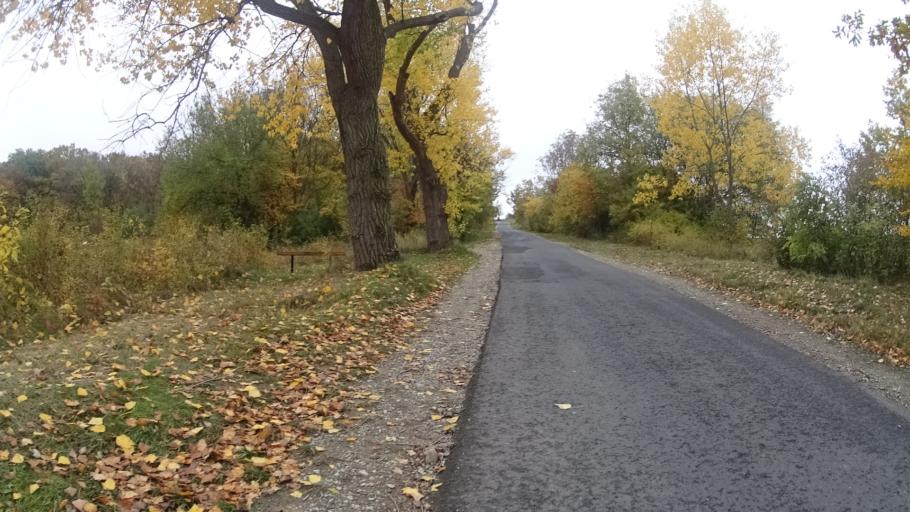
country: DE
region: Thuringia
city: Gossel
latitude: 50.8455
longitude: 10.8813
